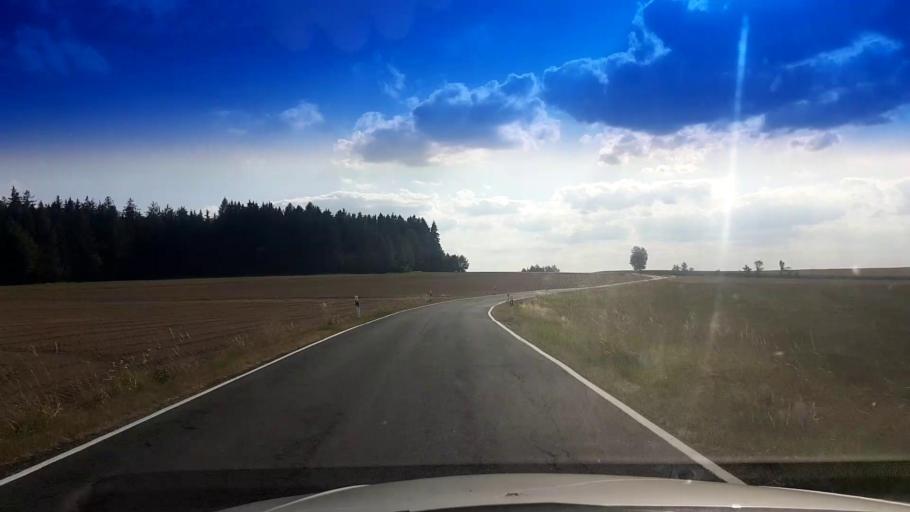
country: DE
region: Bavaria
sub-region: Upper Palatinate
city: Neualbenreuth
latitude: 49.9193
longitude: 12.4021
